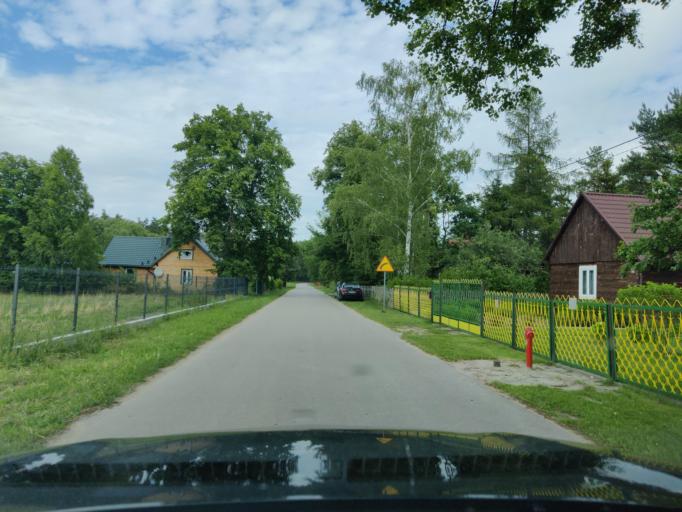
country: PL
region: Masovian Voivodeship
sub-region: Powiat pultuski
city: Obryte
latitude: 52.7373
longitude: 21.1723
